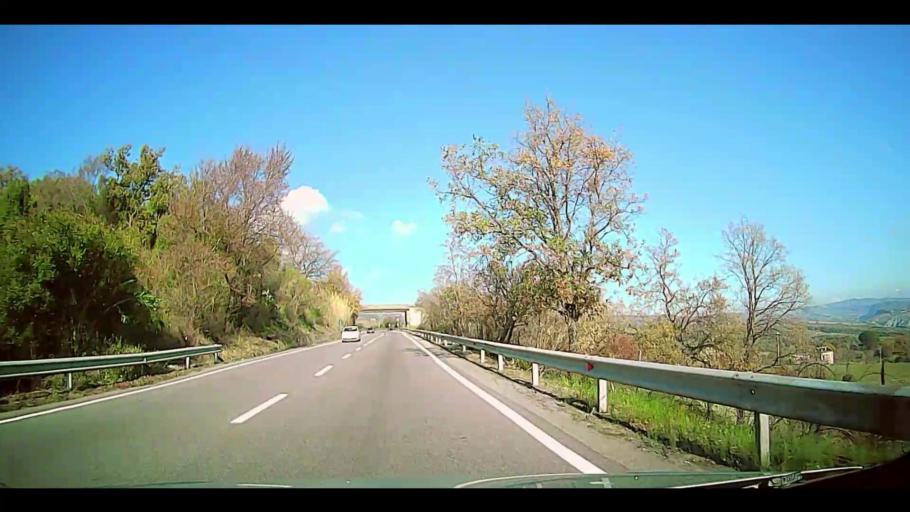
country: IT
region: Calabria
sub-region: Provincia di Crotone
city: Caccuri
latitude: 39.2059
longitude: 16.8055
